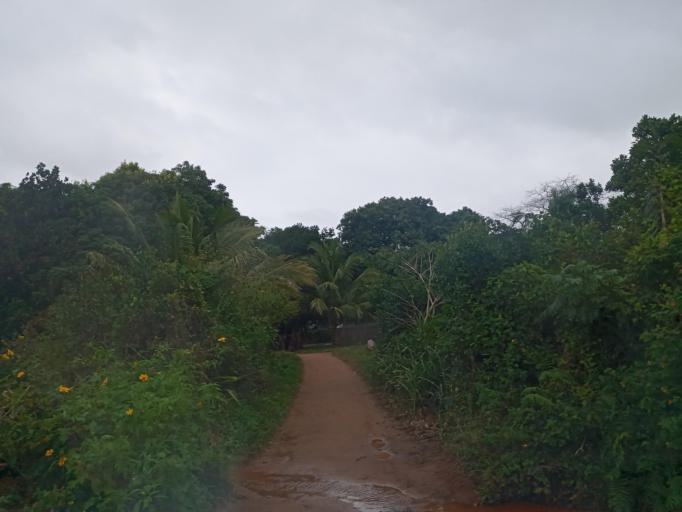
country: MG
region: Atsimo-Atsinanana
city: Vohipaho
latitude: -24.0425
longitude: 47.4399
